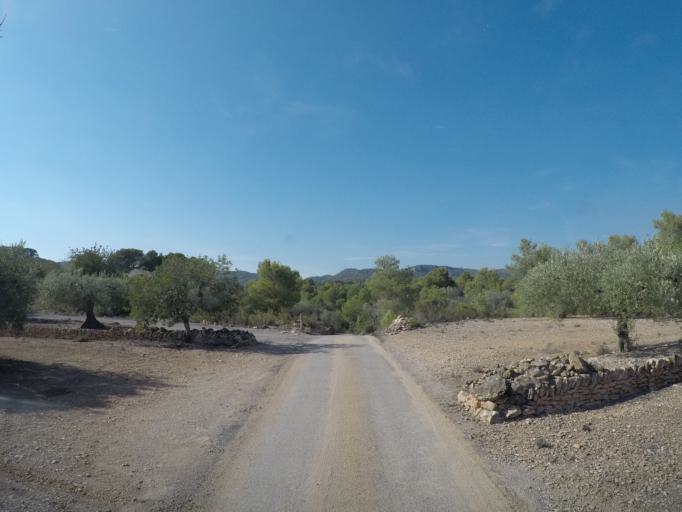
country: ES
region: Catalonia
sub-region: Provincia de Tarragona
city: El Perello
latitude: 40.9041
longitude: 0.7272
